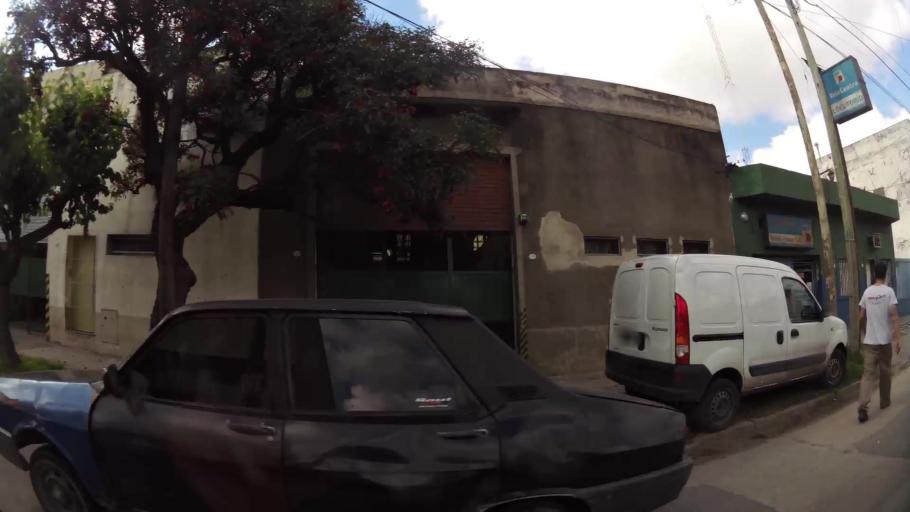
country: AR
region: Buenos Aires
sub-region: Partido de Lanus
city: Lanus
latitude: -34.6893
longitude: -58.4234
